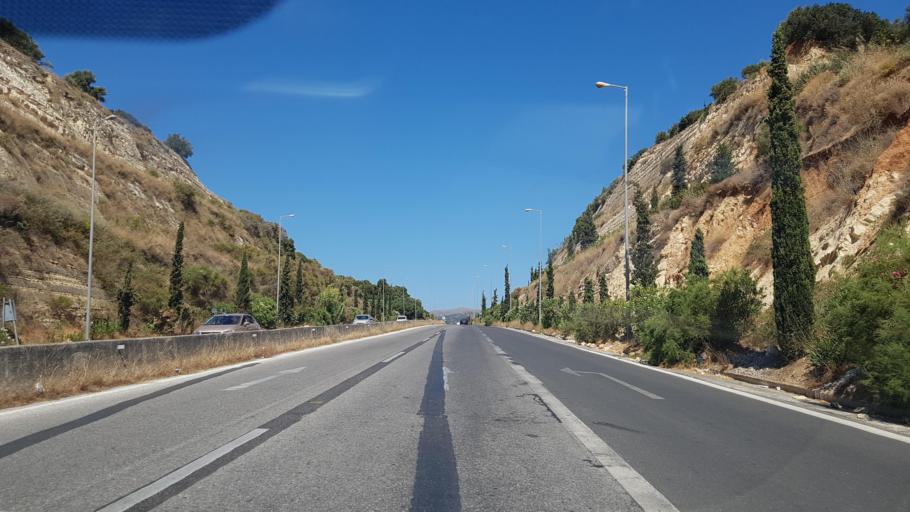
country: GR
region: Crete
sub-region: Nomos Chanias
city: Kolympari
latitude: 35.5208
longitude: 23.8168
